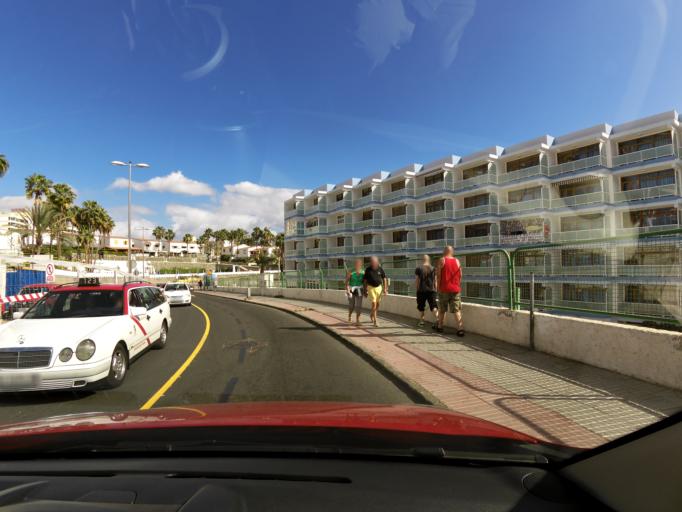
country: ES
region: Canary Islands
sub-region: Provincia de Las Palmas
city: Playa del Ingles
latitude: 27.7583
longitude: -15.5734
